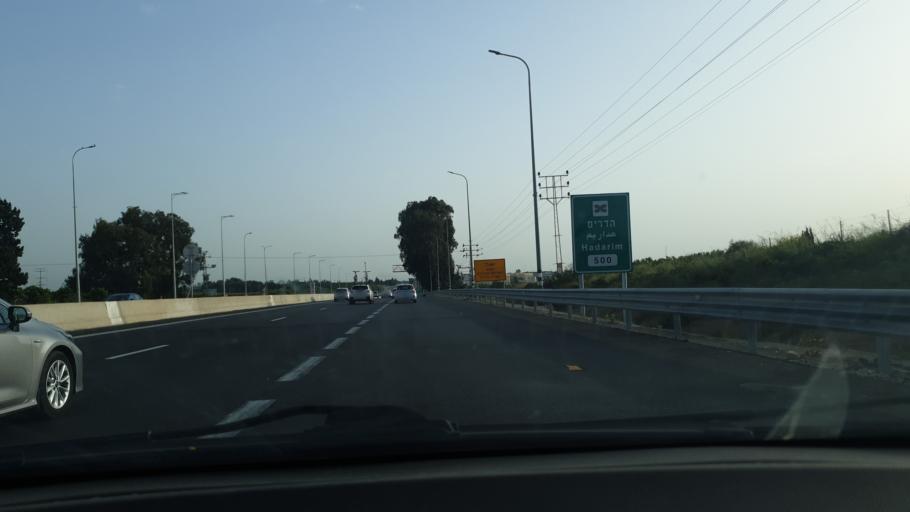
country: IL
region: Central District
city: Even Yehuda
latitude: 32.2479
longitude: 34.8889
